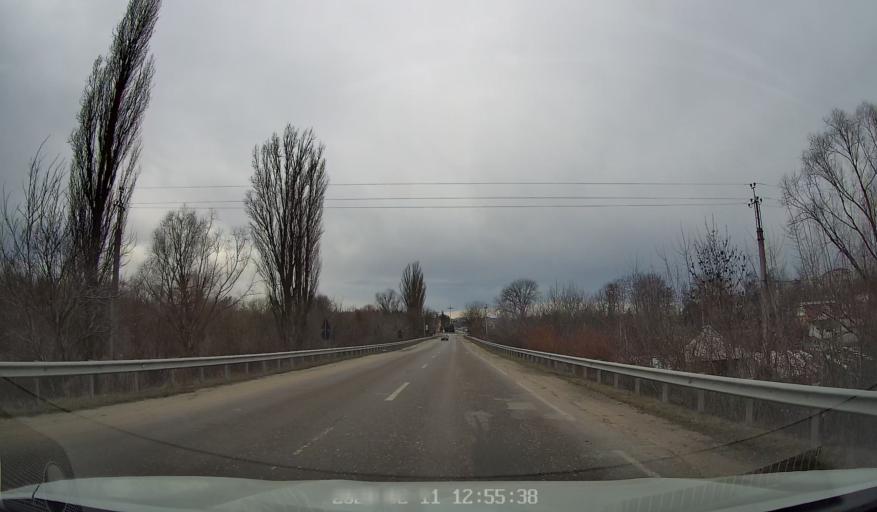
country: MD
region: Briceni
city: Briceni
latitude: 48.3512
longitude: 27.0886
